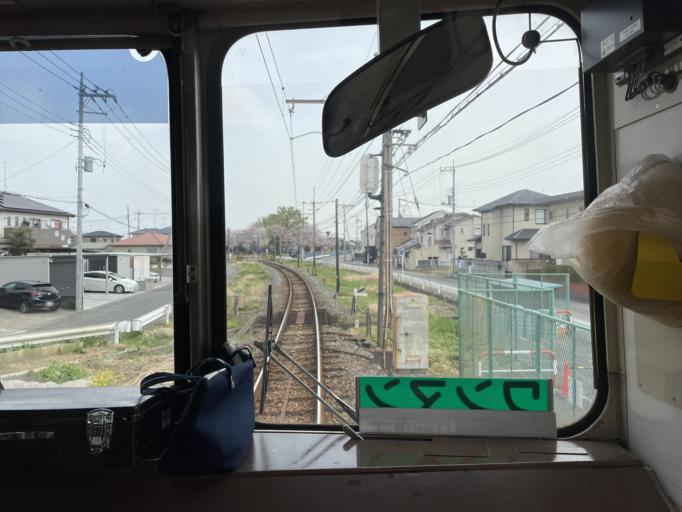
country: JP
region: Saitama
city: Gyoda
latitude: 36.1384
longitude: 139.4437
